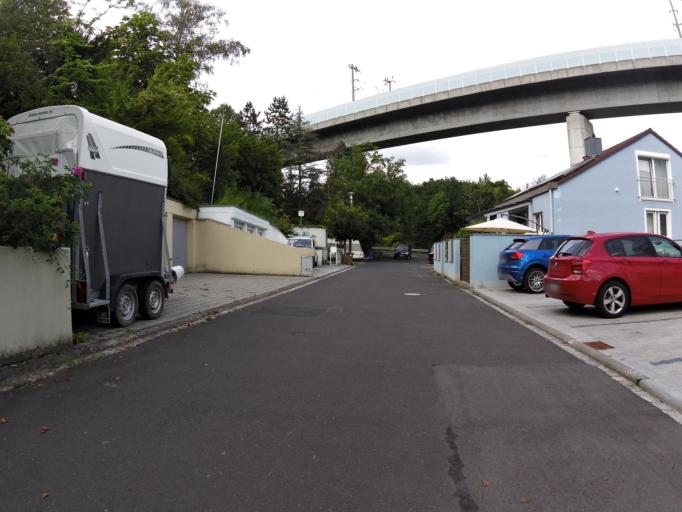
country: DE
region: Bavaria
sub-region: Regierungsbezirk Unterfranken
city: Margetshochheim
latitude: 49.8275
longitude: 9.8658
